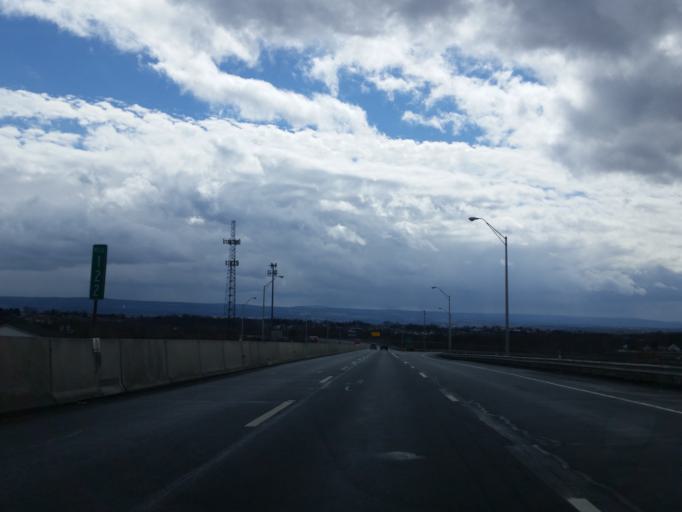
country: US
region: Pennsylvania
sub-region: Lackawanna County
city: Old Forge
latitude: 41.3937
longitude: -75.7319
